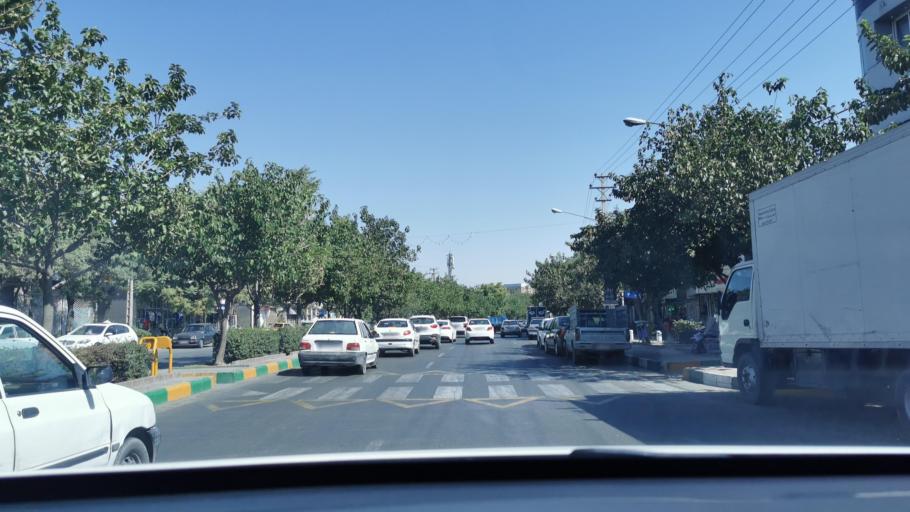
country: IR
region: Razavi Khorasan
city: Mashhad
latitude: 36.3395
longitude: 59.6250
